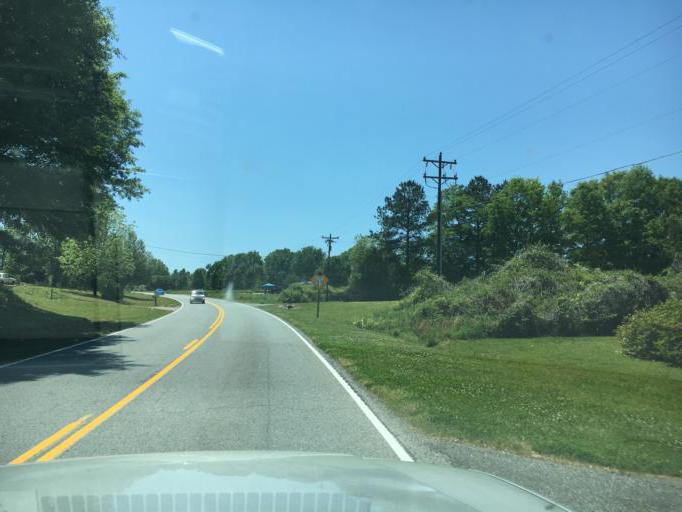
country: US
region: South Carolina
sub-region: Cherokee County
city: East Gaffney
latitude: 35.1178
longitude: -81.5984
